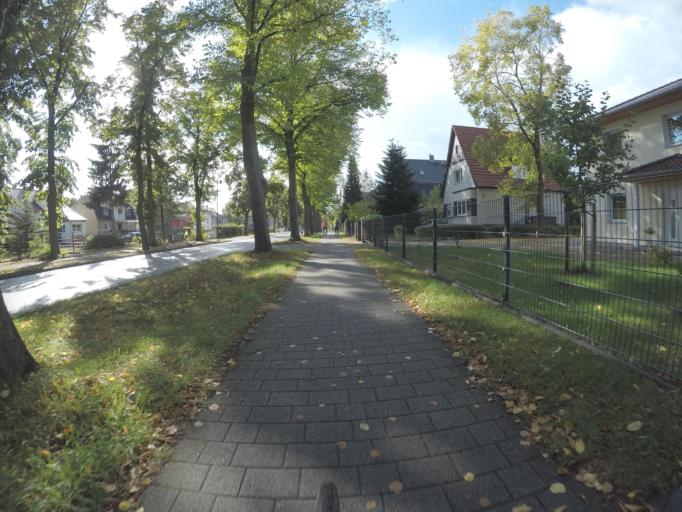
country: DE
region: Brandenburg
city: Petershagen
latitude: 52.5245
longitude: 13.7745
